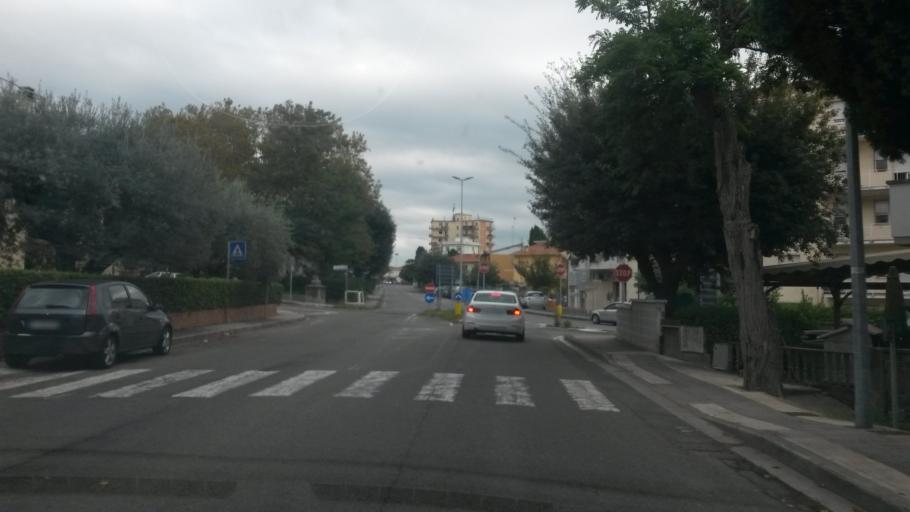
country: IT
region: Tuscany
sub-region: Provincia di Livorno
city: Rosignano Solvay-Castiglioncello
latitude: 43.3989
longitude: 10.4416
